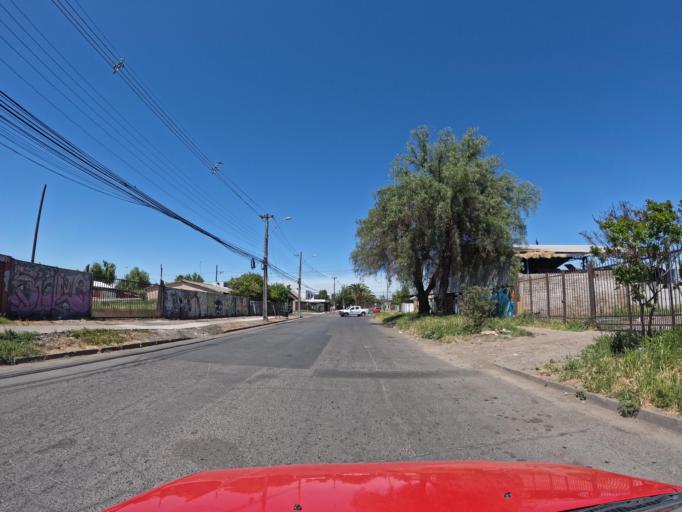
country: CL
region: Maule
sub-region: Provincia de Curico
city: Curico
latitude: -34.9775
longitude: -71.2529
